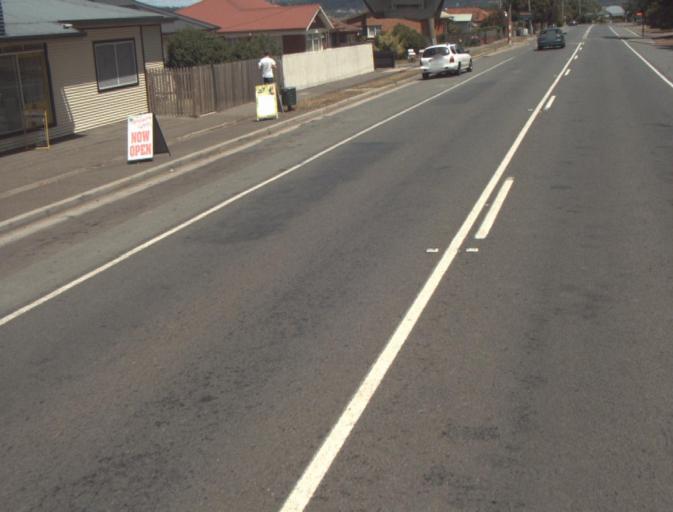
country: AU
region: Tasmania
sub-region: Launceston
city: Mayfield
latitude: -41.3771
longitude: 147.1293
